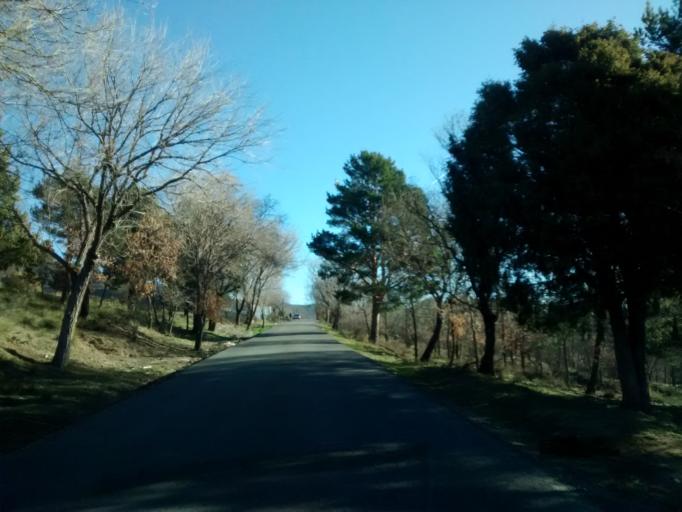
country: ES
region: Madrid
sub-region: Provincia de Madrid
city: Navacerrada
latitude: 40.7392
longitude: -4.0065
